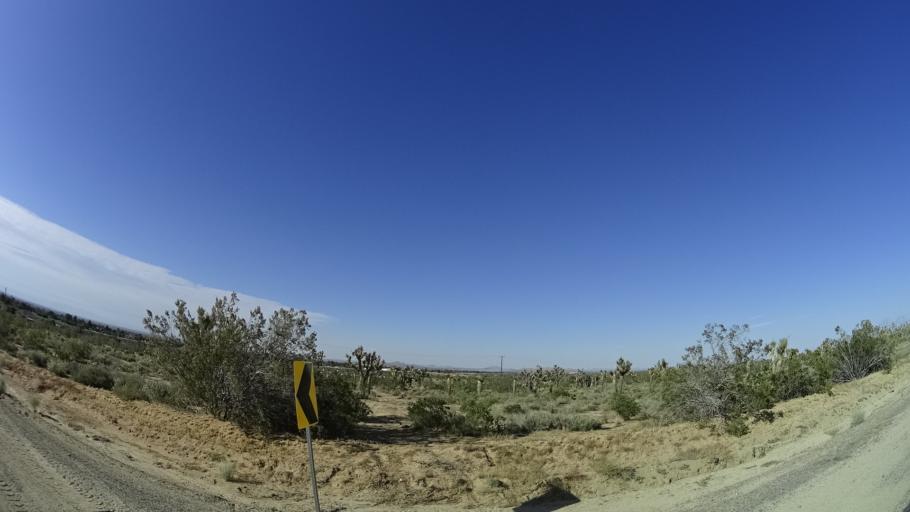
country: US
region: California
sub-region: Los Angeles County
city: Littlerock
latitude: 34.5127
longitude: -117.9790
